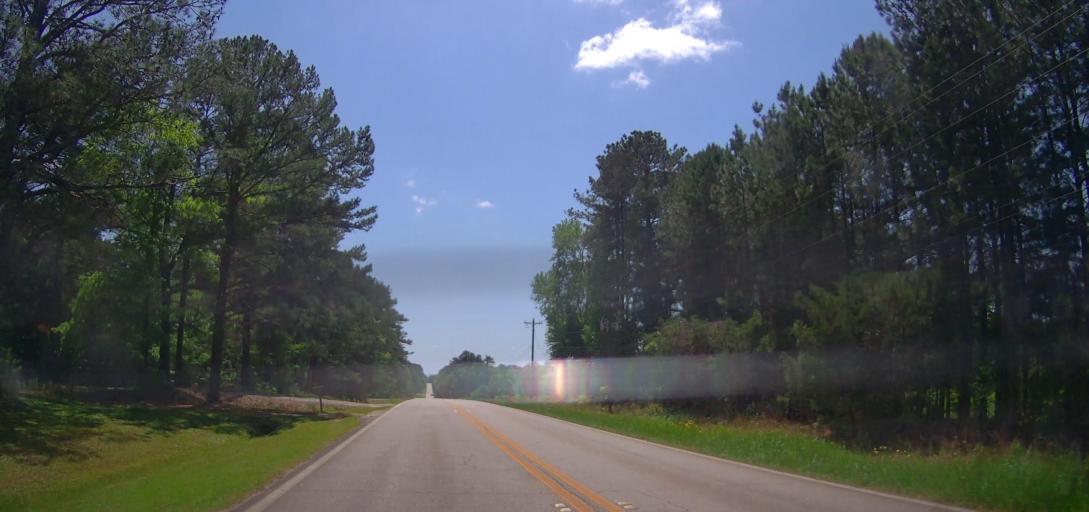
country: US
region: Georgia
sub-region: Jones County
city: Gray
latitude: 33.0508
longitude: -83.5956
